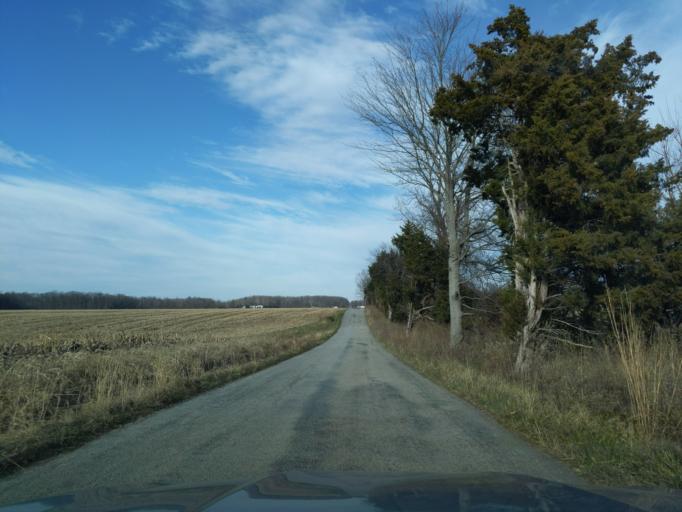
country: US
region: Indiana
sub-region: Decatur County
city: Greensburg
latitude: 39.2156
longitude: -85.4298
